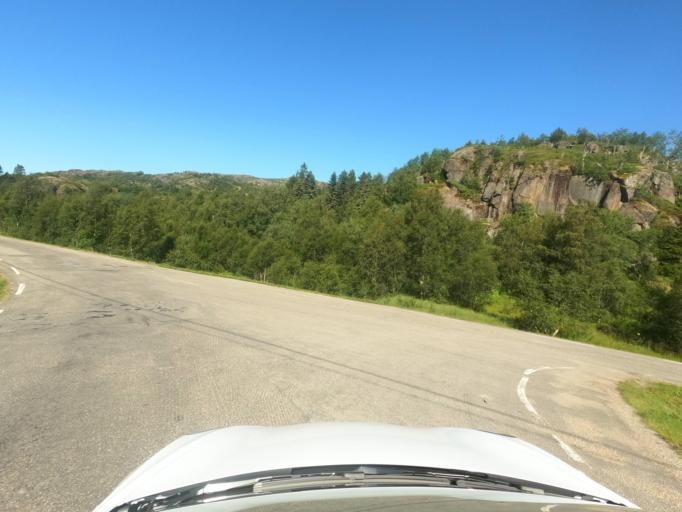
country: NO
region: Nordland
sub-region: Hadsel
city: Stokmarknes
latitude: 68.3028
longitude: 15.0410
